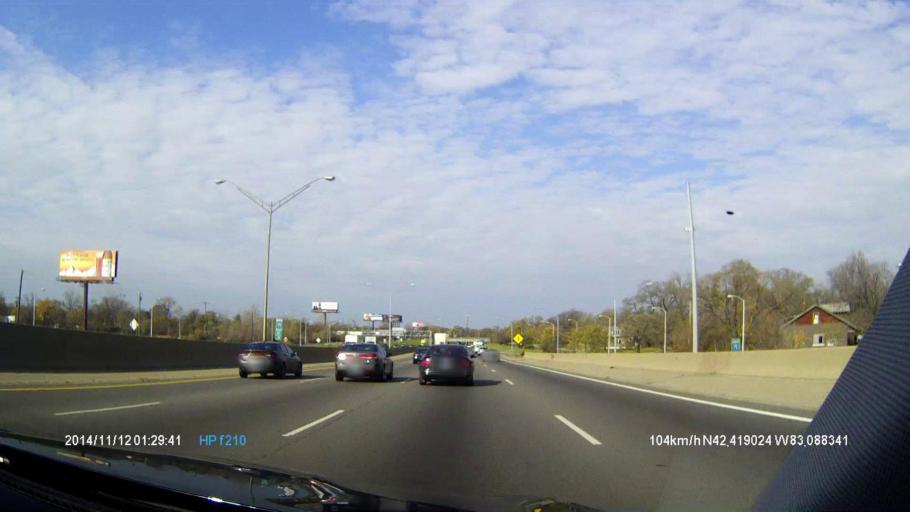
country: US
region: Michigan
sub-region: Wayne County
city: Highland Park
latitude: 42.4191
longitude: -83.0879
